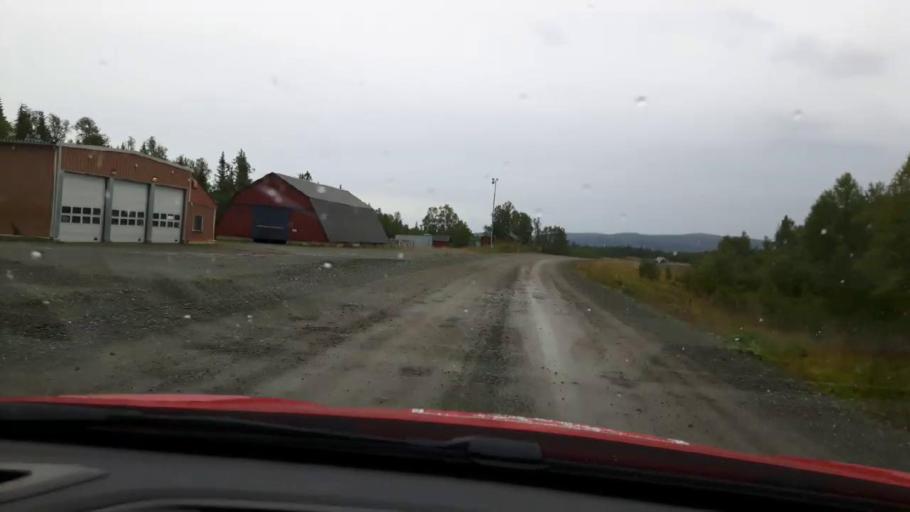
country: NO
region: Nord-Trondelag
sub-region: Meraker
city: Meraker
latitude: 63.5689
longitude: 12.2855
